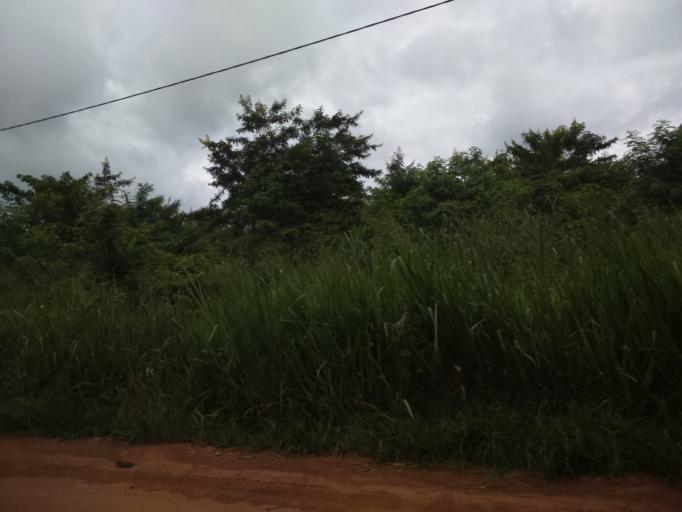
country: CI
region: Moyen-Comoe
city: Abengourou
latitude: 6.6319
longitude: -3.7102
